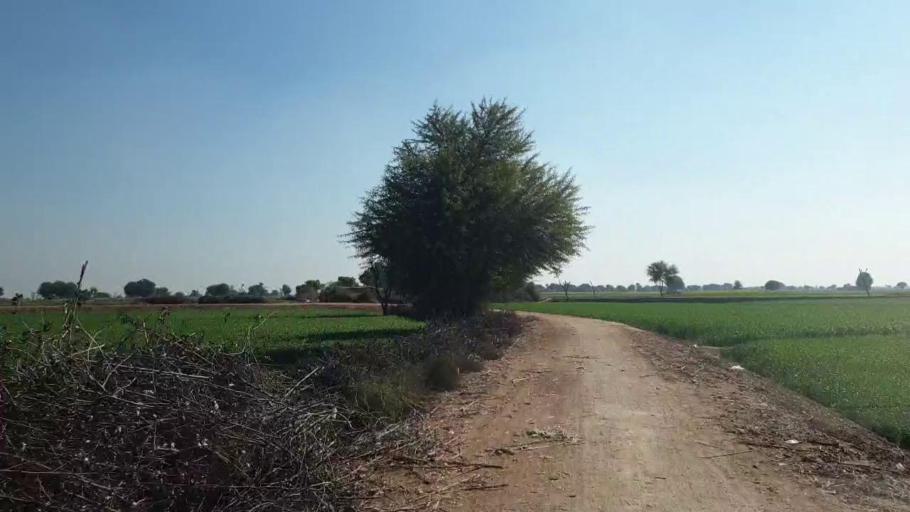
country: PK
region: Sindh
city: Shahpur Chakar
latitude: 26.1233
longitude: 68.6442
